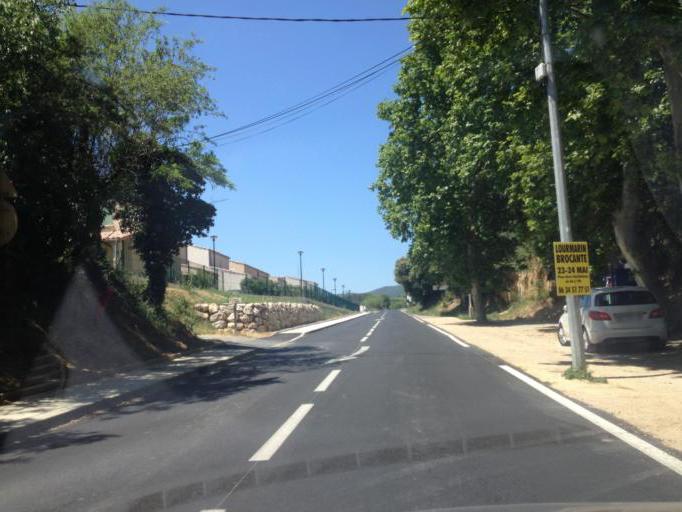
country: FR
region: Provence-Alpes-Cote d'Azur
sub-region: Departement du Vaucluse
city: Cadenet
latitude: 43.7384
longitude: 5.3655
